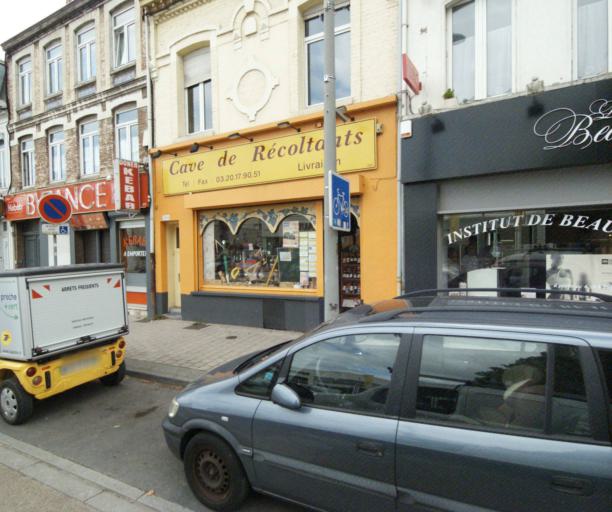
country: FR
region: Nord-Pas-de-Calais
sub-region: Departement du Nord
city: Lambersart
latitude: 50.6367
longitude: 3.0253
